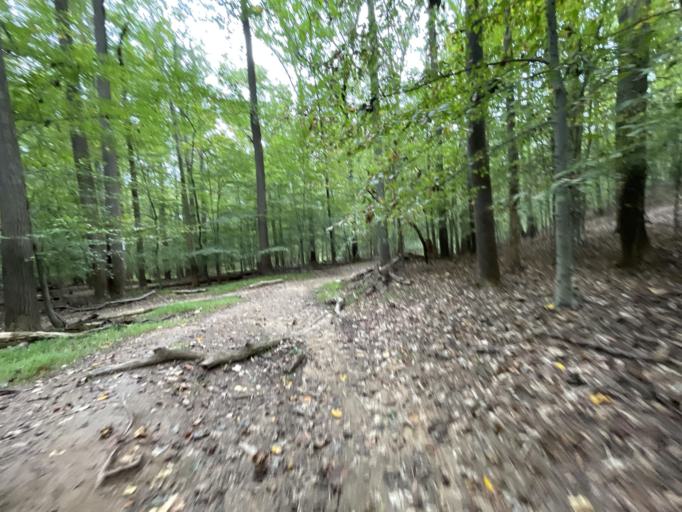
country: US
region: Maryland
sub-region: Baltimore County
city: Hampton
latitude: 39.4327
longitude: -76.5695
